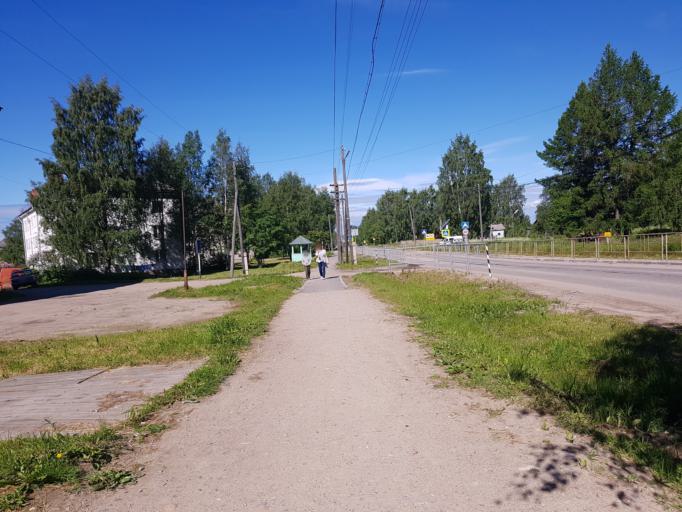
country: RU
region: Republic of Karelia
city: Kalevala
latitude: 65.1962
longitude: 31.2014
